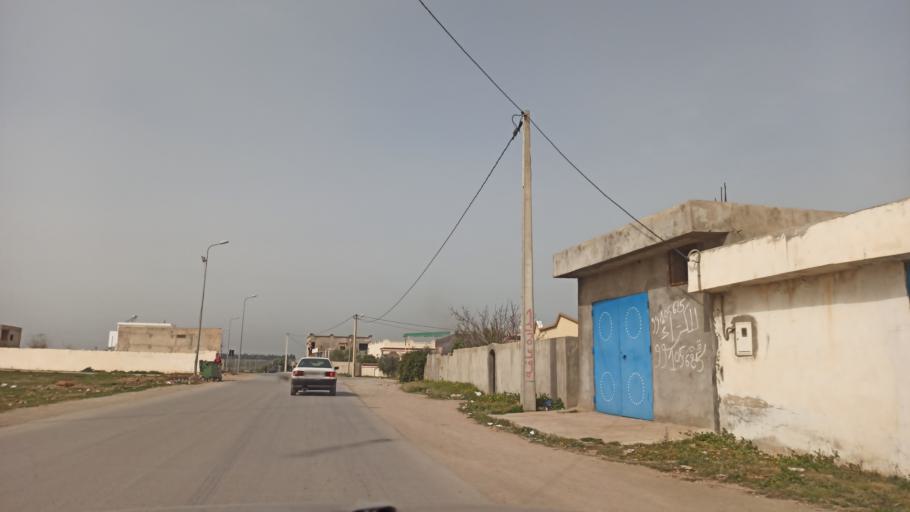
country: TN
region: Zaghwan
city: Zaghouan
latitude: 36.4174
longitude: 10.1209
